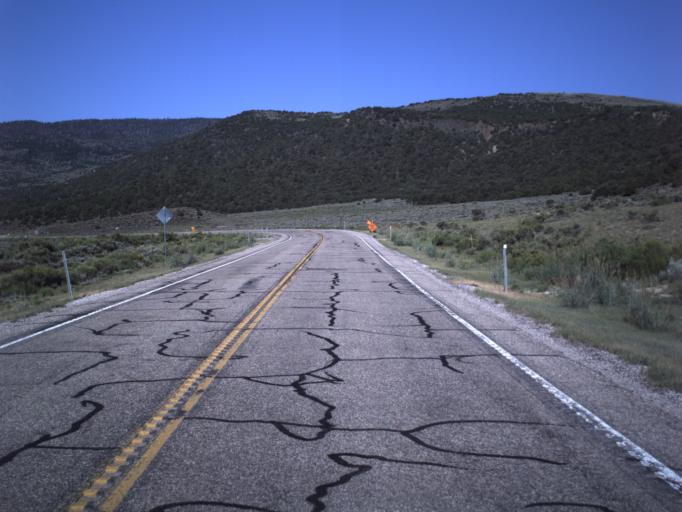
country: US
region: Utah
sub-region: Wayne County
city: Loa
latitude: 38.6364
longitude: -111.4361
